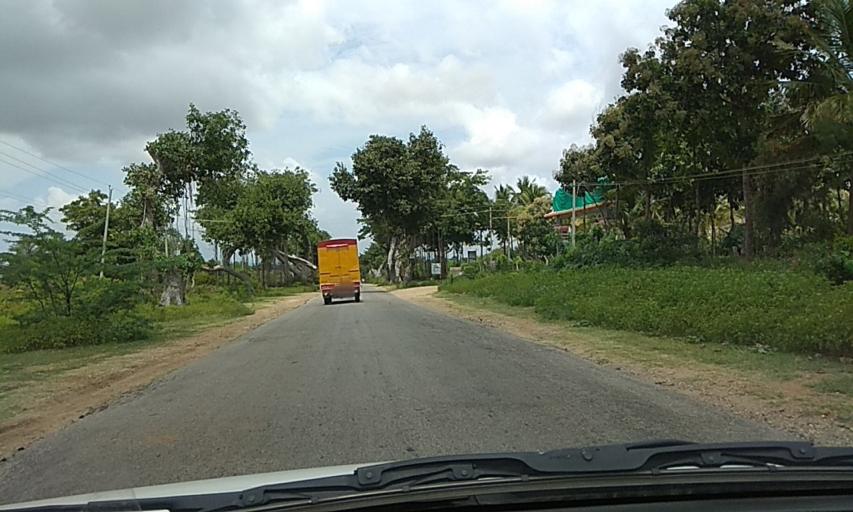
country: IN
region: Karnataka
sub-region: Chamrajnagar
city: Gundlupet
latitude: 11.8121
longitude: 76.7705
